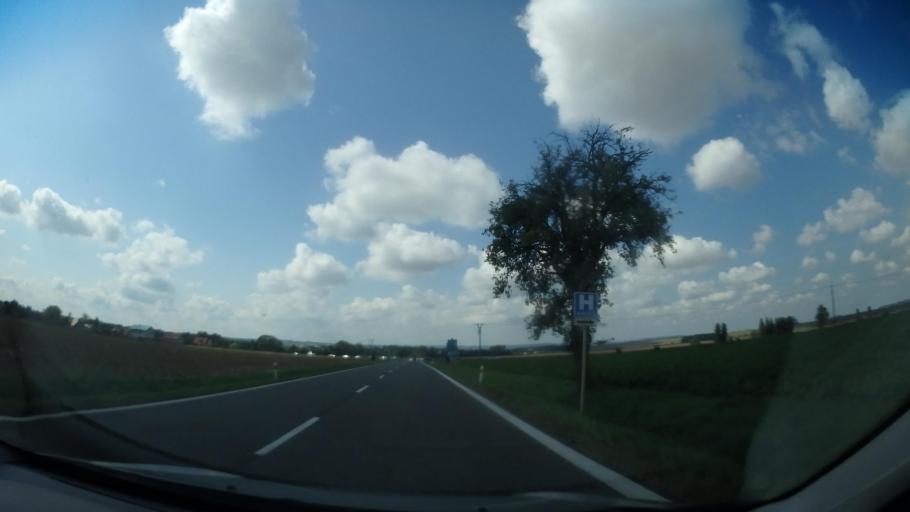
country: CZ
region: Central Bohemia
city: Suchdol
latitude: 49.9559
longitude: 15.1043
